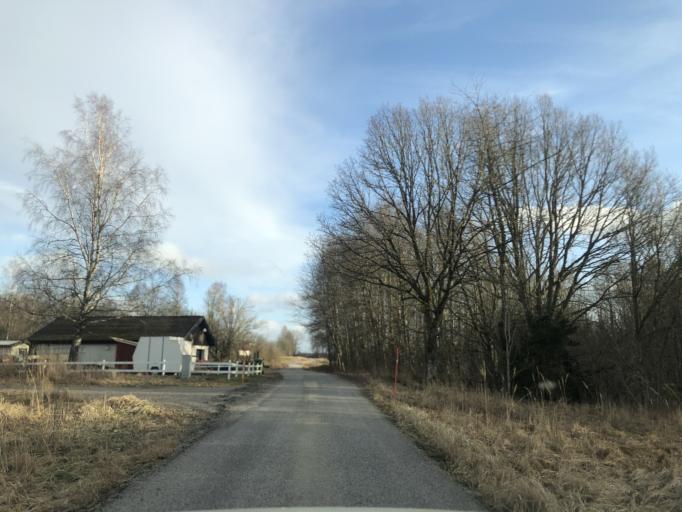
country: SE
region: Vaestra Goetaland
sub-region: Ulricehamns Kommun
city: Ulricehamn
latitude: 57.8108
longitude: 13.3608
